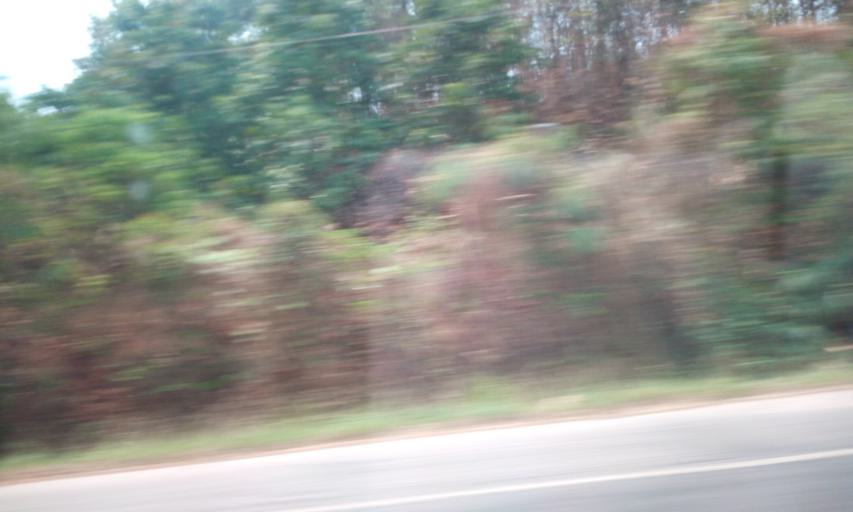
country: TH
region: Chiang Rai
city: Pa Daet
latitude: 19.6420
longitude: 99.9547
